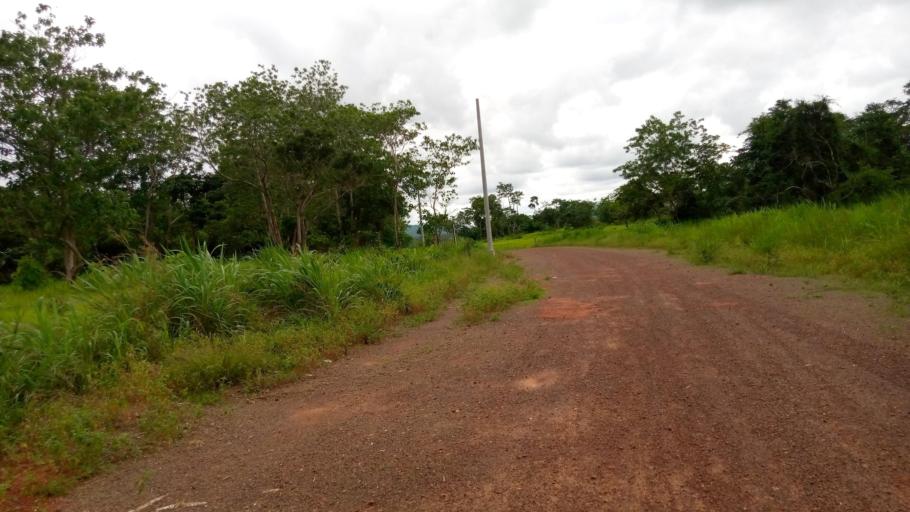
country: SL
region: Southern Province
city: Moyamba
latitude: 8.1601
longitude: -12.4492
